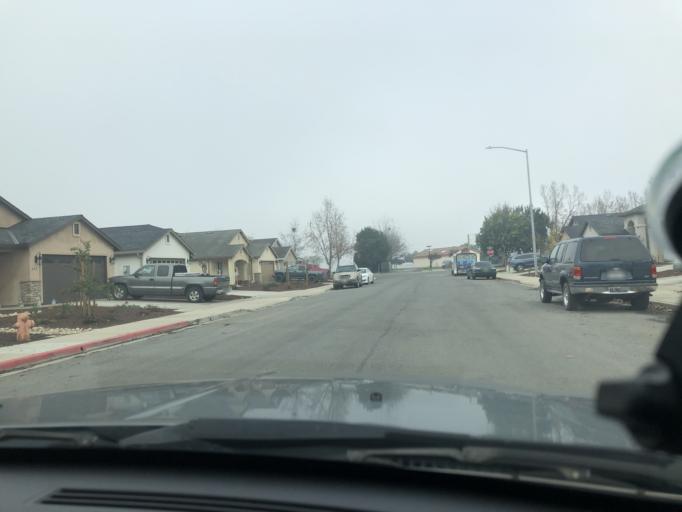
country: US
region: California
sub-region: Monterey County
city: King City
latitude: 36.2084
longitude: -121.1412
